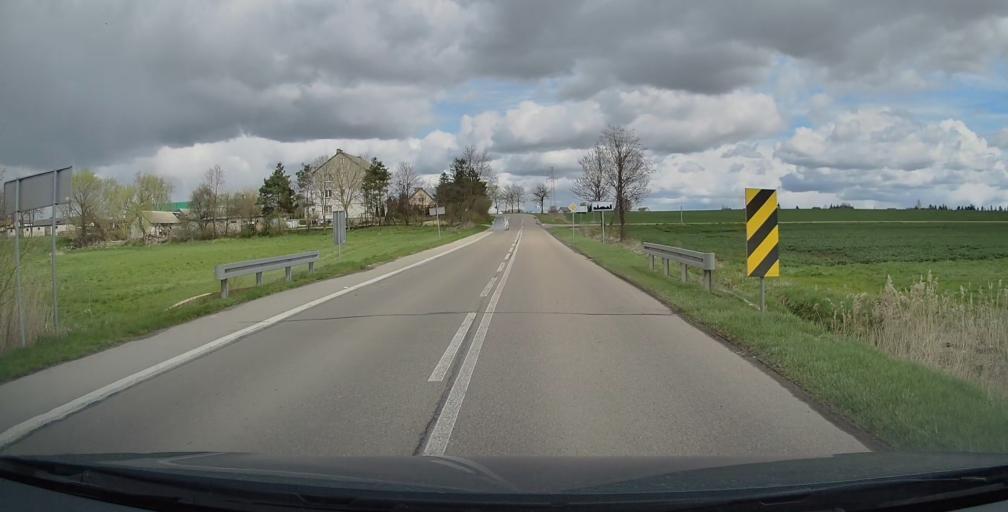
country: PL
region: Masovian Voivodeship
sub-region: Powiat ostrolecki
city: Goworowo
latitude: 52.8754
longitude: 21.5667
